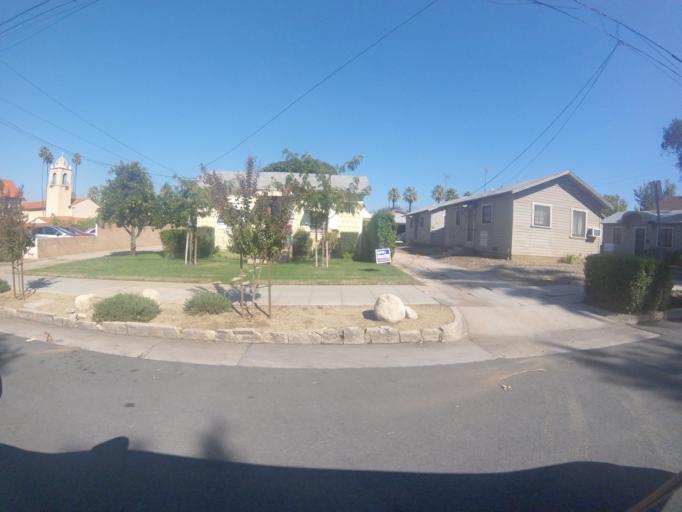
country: US
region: California
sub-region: San Bernardino County
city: Redlands
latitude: 34.0520
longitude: -117.1815
